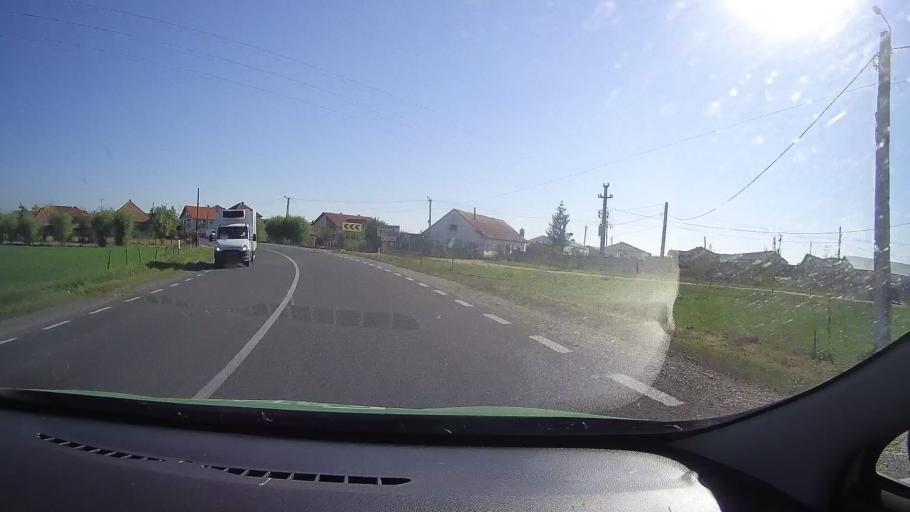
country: RO
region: Satu Mare
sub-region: Oras Ardud
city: Ardud
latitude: 47.6540
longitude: 22.8864
